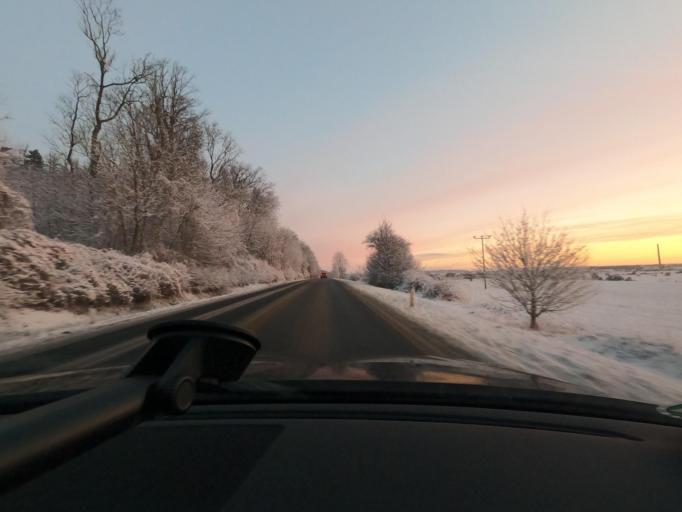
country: DE
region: Thuringia
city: Kallmerode
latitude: 51.3676
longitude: 10.3071
